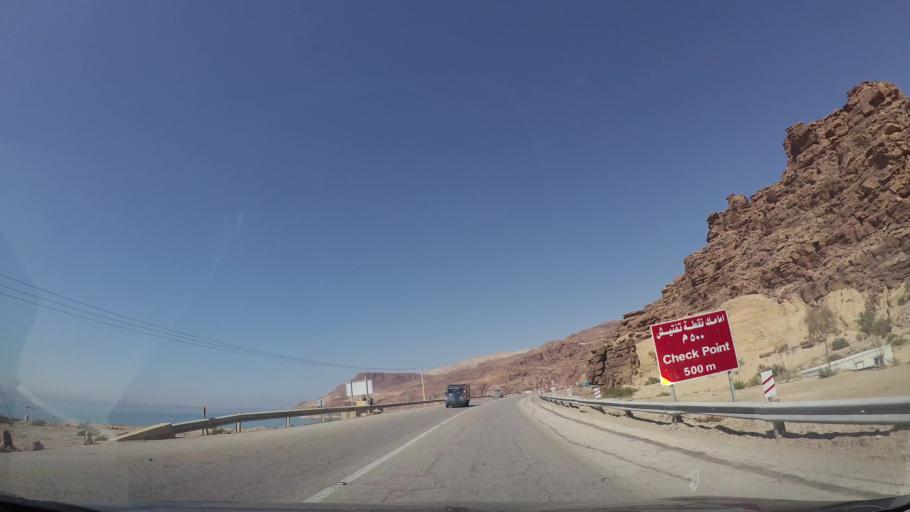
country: JO
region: Karak
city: Al Qasr
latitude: 31.4681
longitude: 35.5728
